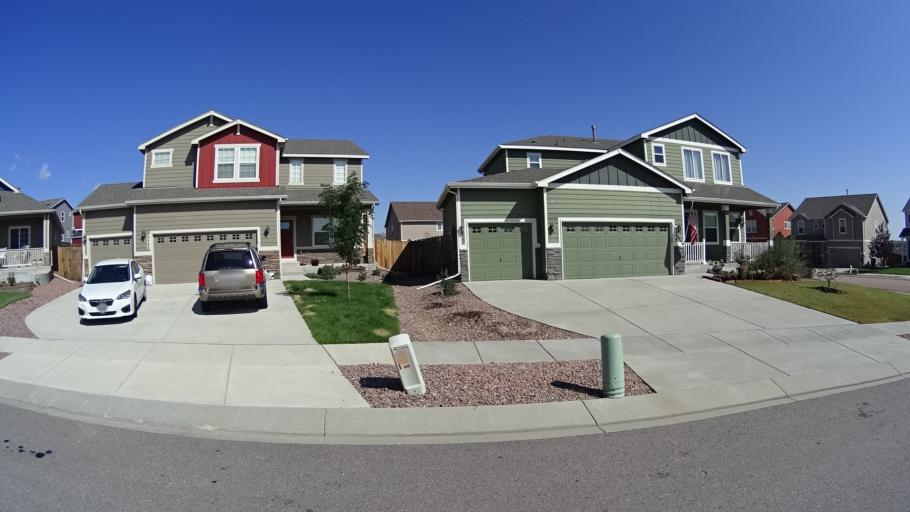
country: US
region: Colorado
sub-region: El Paso County
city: Cimarron Hills
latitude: 38.9273
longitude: -104.7075
